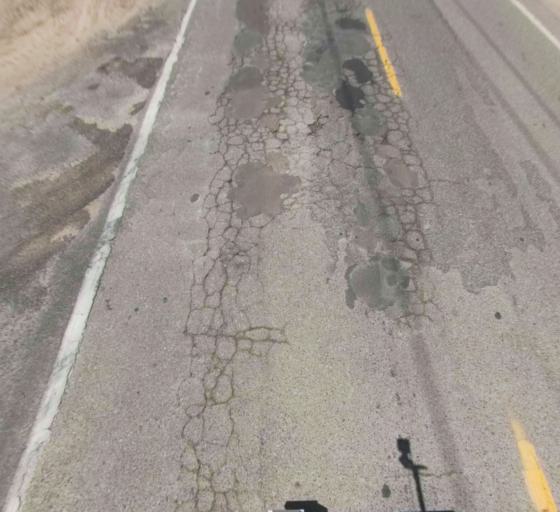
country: US
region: California
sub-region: Fresno County
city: Biola
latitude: 36.8658
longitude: -119.9113
